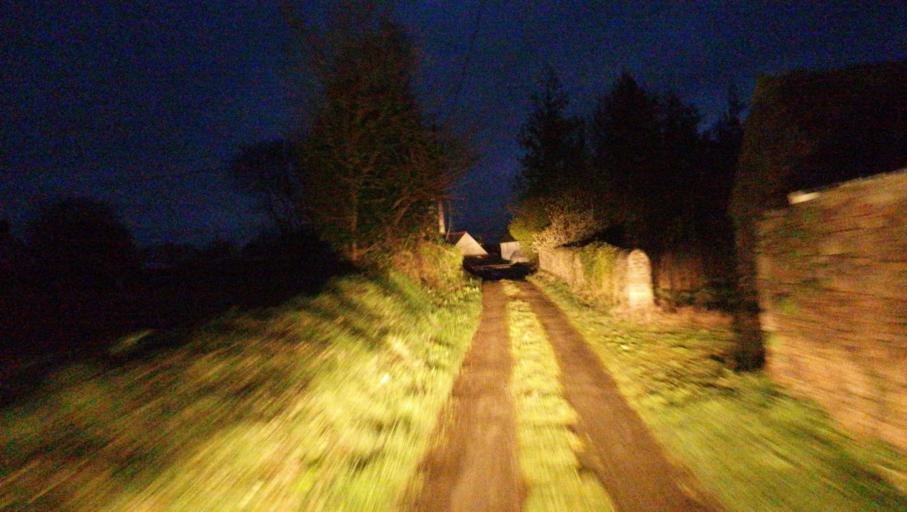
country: FR
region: Brittany
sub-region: Departement des Cotes-d'Armor
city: Plehedel
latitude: 48.6811
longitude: -3.0322
